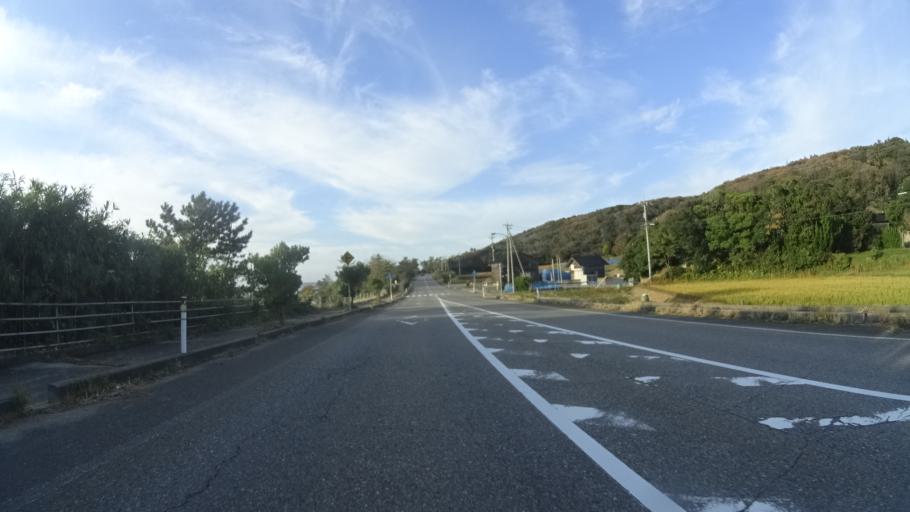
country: JP
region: Ishikawa
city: Hakui
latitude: 37.1039
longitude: 136.7305
